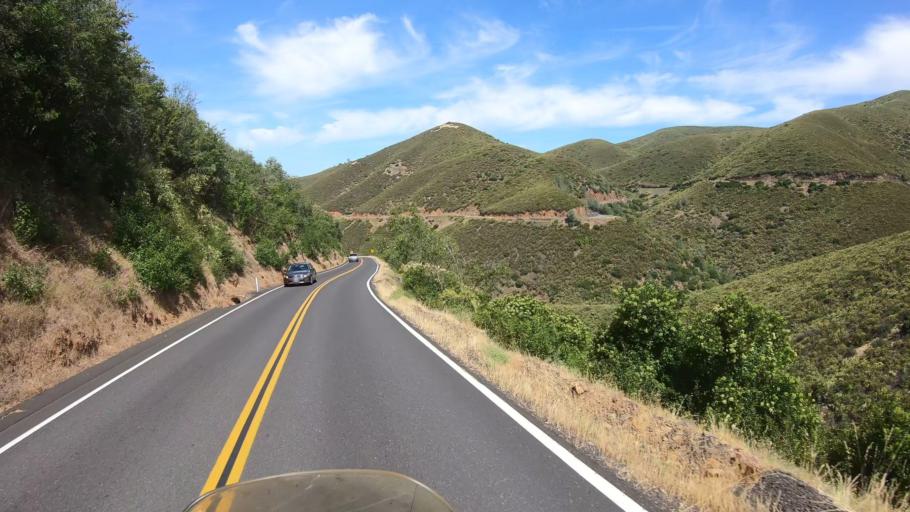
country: US
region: California
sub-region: Tuolumne County
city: Tuolumne City
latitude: 37.8182
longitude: -120.2803
